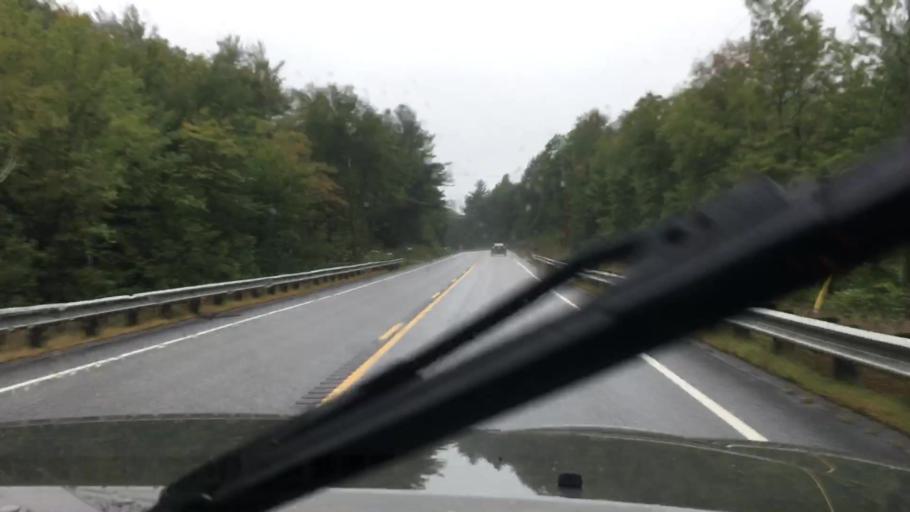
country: US
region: New Hampshire
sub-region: Cheshire County
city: Harrisville
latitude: 43.0373
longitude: -72.0998
